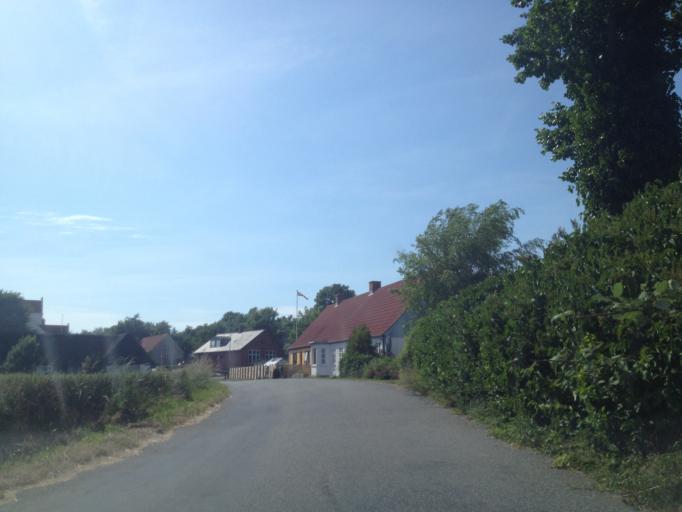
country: DK
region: Central Jutland
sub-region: Samso Kommune
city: Tranebjerg
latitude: 55.8004
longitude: 10.5606
